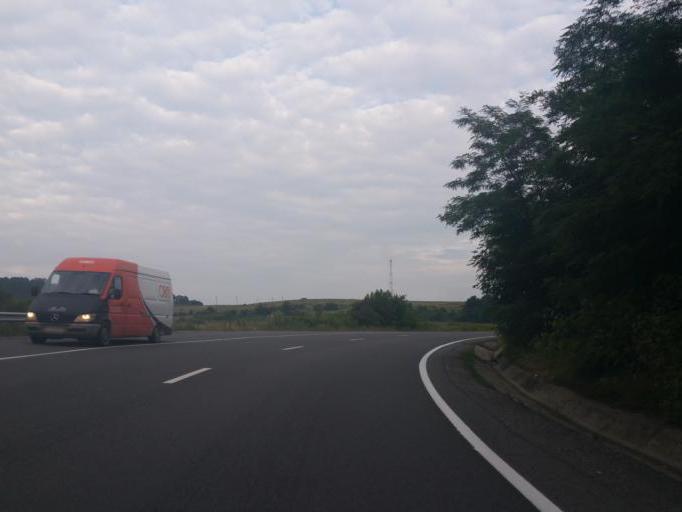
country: RO
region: Salaj
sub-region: Comuna Dragu
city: Dragu
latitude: 46.9469
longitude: 23.3763
